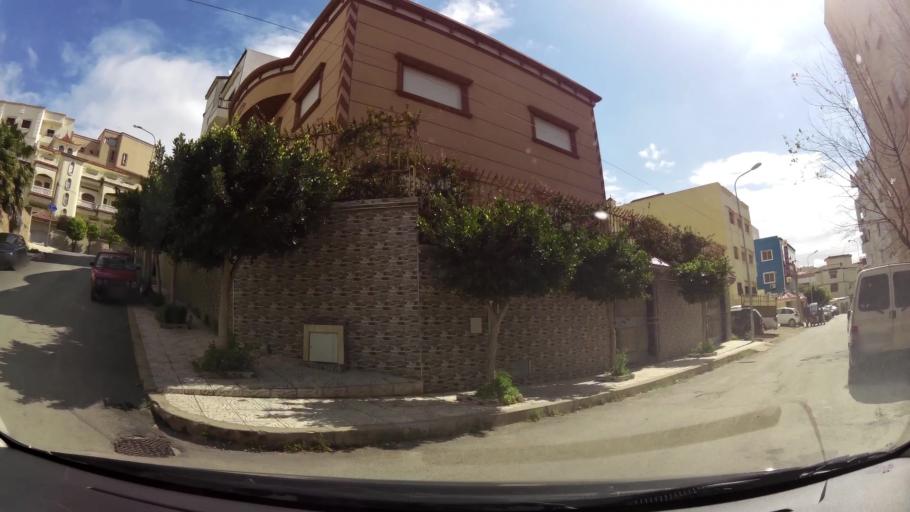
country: MA
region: Tanger-Tetouan
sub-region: Tanger-Assilah
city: Tangier
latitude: 35.7739
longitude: -5.8307
